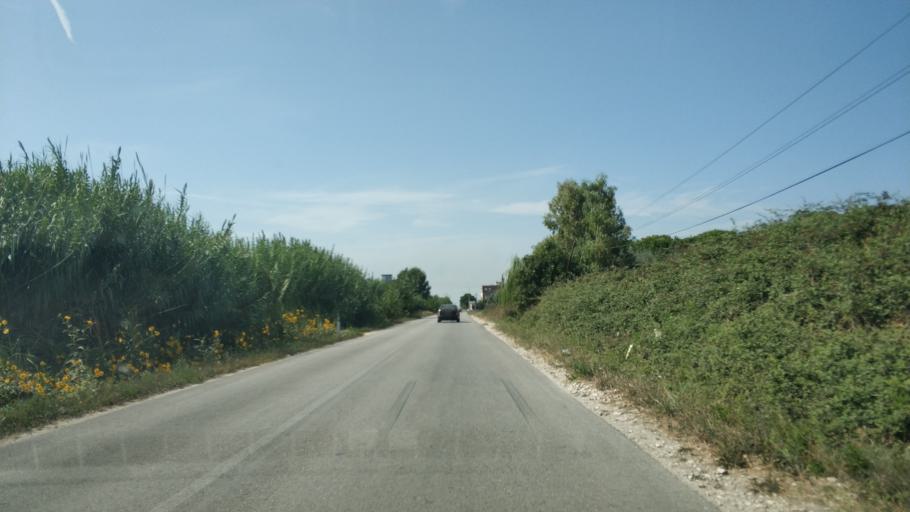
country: AL
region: Fier
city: Fier
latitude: 40.7348
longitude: 19.5270
